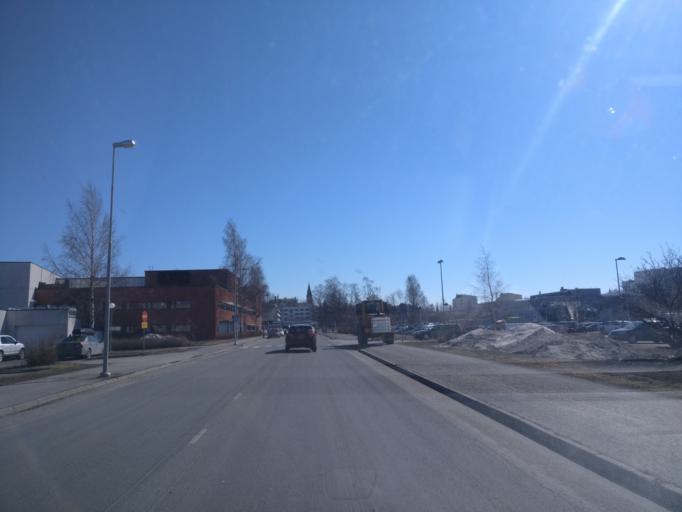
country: FI
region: Lapland
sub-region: Kemi-Tornio
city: Kemi
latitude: 65.7363
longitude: 24.5549
